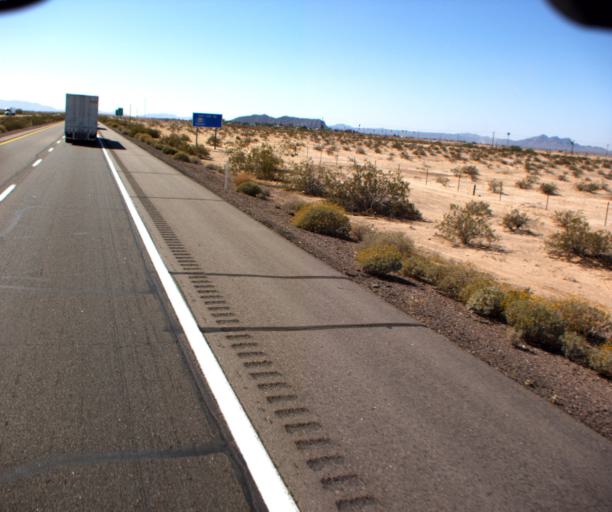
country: US
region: Arizona
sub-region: Yuma County
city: Wellton
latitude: 32.6970
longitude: -113.9315
